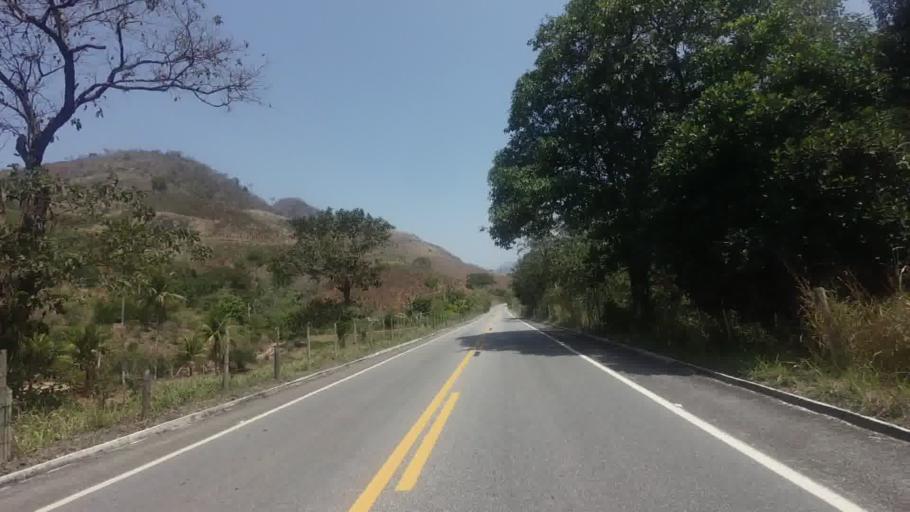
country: BR
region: Espirito Santo
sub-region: Cachoeiro De Itapemirim
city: Cachoeiro de Itapemirim
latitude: -20.8504
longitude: -41.2437
